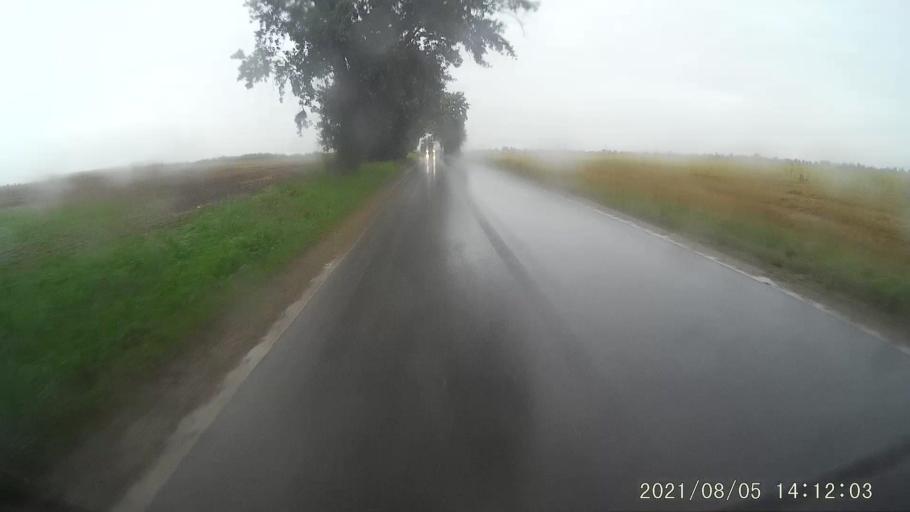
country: PL
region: Opole Voivodeship
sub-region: Powiat krapkowicki
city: Strzeleczki
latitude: 50.4698
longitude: 17.7671
